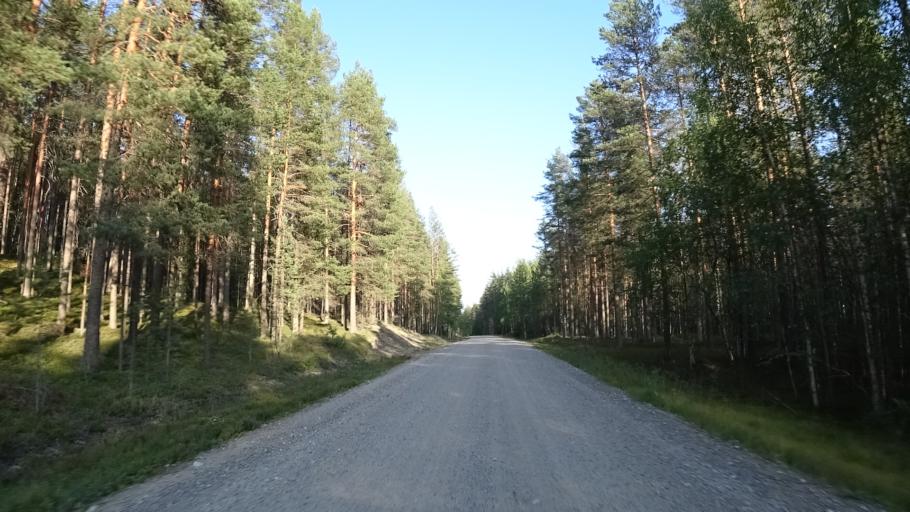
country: FI
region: North Karelia
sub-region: Joensuu
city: Ilomantsi
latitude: 63.1388
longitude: 30.6954
